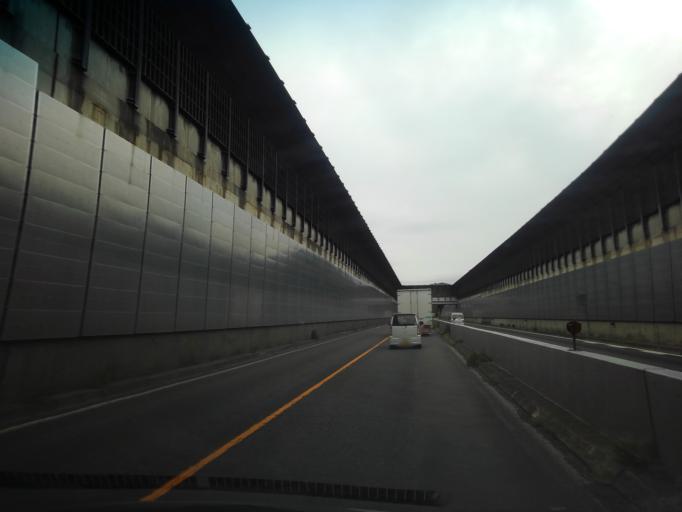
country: JP
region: Tokyo
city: Hachioji
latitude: 35.6275
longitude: 139.3490
